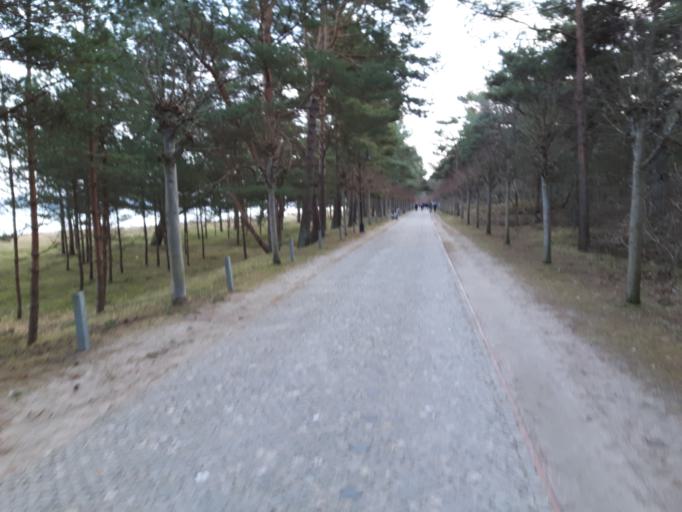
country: DE
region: Mecklenburg-Vorpommern
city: Ostseebad Binz
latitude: 54.4168
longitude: 13.5944
